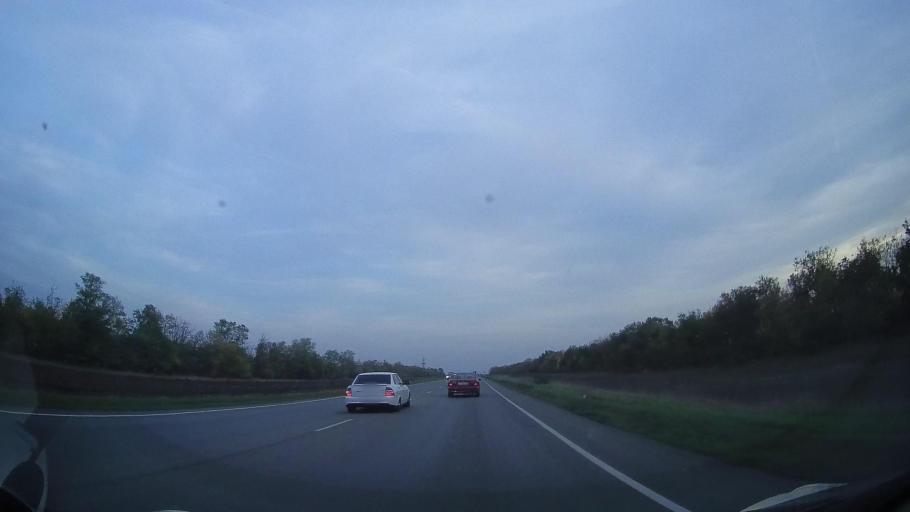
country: RU
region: Rostov
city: Kirovskaya
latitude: 46.9349
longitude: 40.0930
